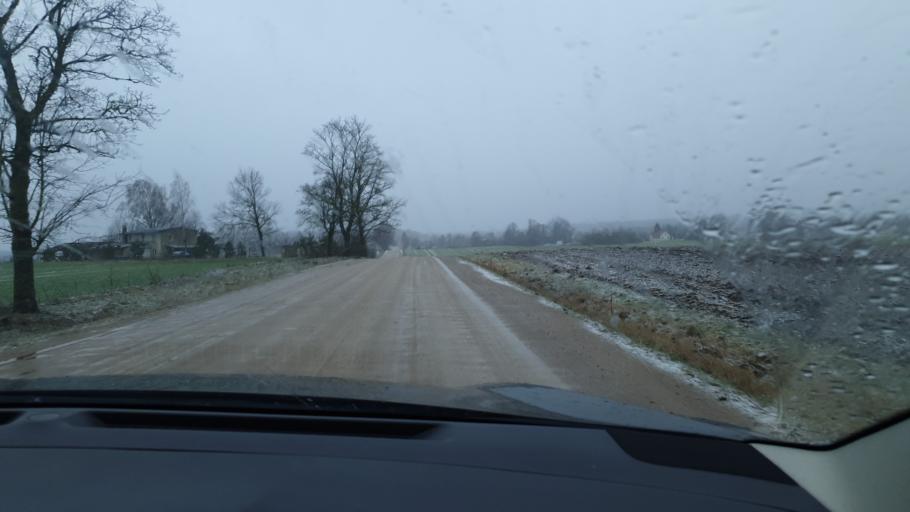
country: LT
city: Jieznas
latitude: 54.5788
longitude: 24.3169
